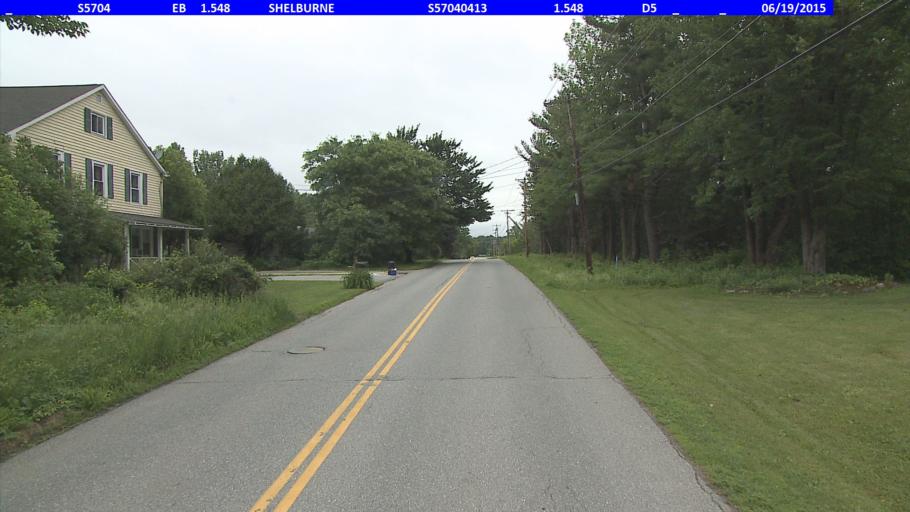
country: US
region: Vermont
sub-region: Chittenden County
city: Burlington
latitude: 44.4040
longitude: -73.2202
